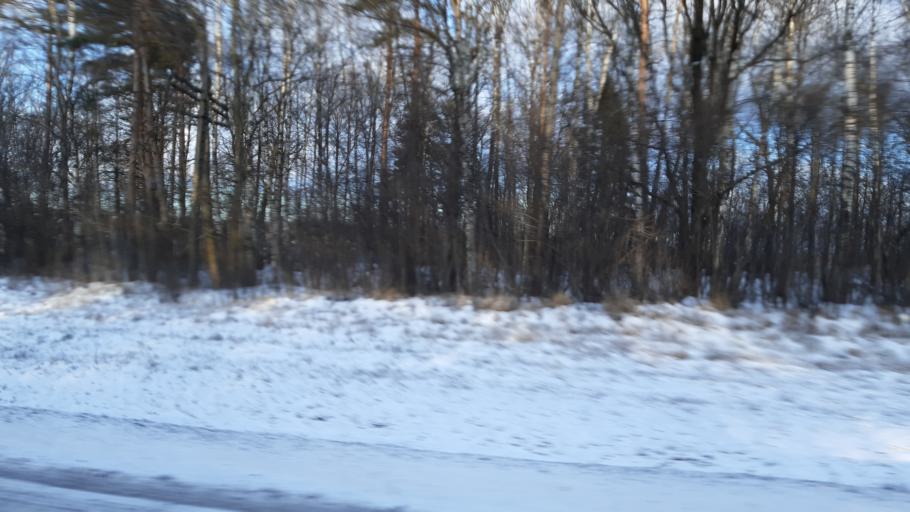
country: RU
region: Moskovskaya
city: Svatkovo
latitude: 56.3083
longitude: 38.3255
